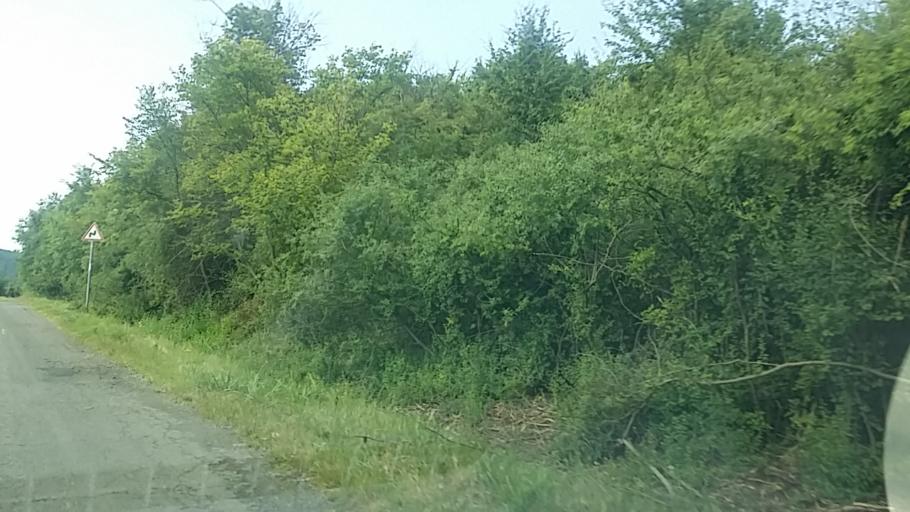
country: HU
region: Nograd
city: Matraverebely
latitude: 47.9698
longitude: 19.7643
